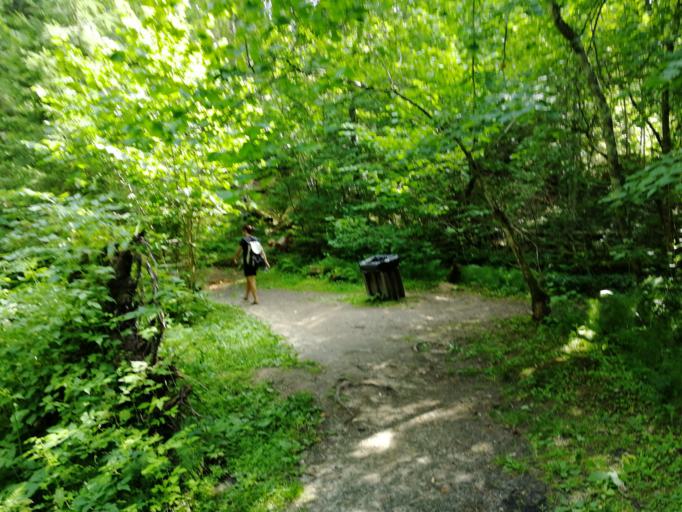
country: LV
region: Cesu Rajons
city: Cesis
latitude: 57.3000
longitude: 25.2193
